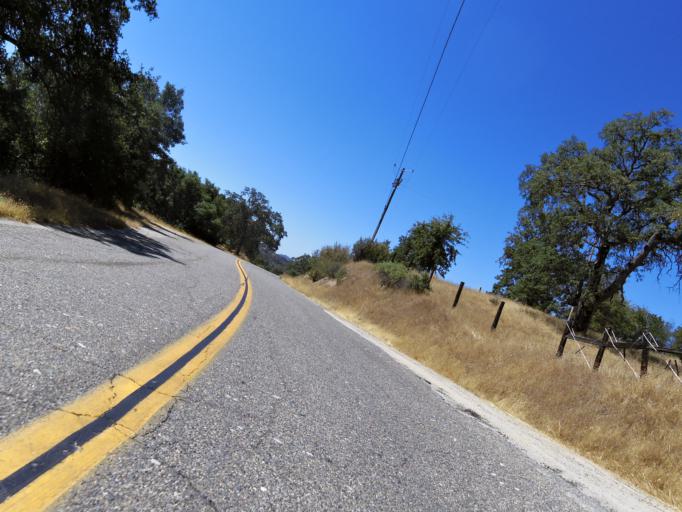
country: US
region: California
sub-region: Fresno County
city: Auberry
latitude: 37.1910
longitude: -119.5035
